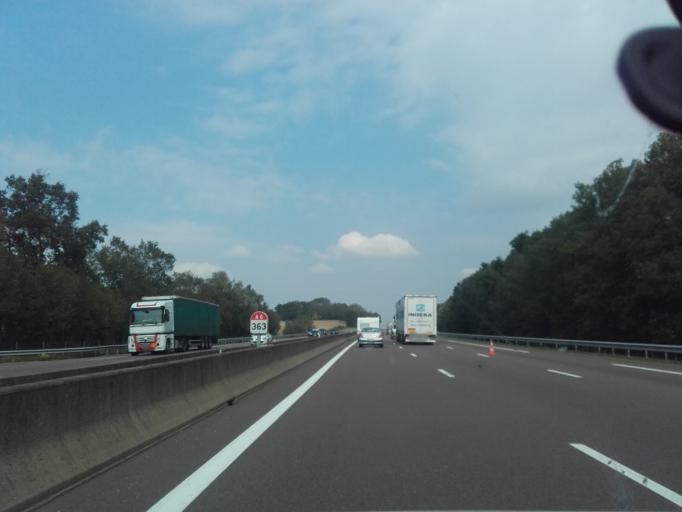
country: FR
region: Bourgogne
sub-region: Departement de Saone-et-Loire
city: Tournus
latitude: 46.5188
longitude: 4.9140
